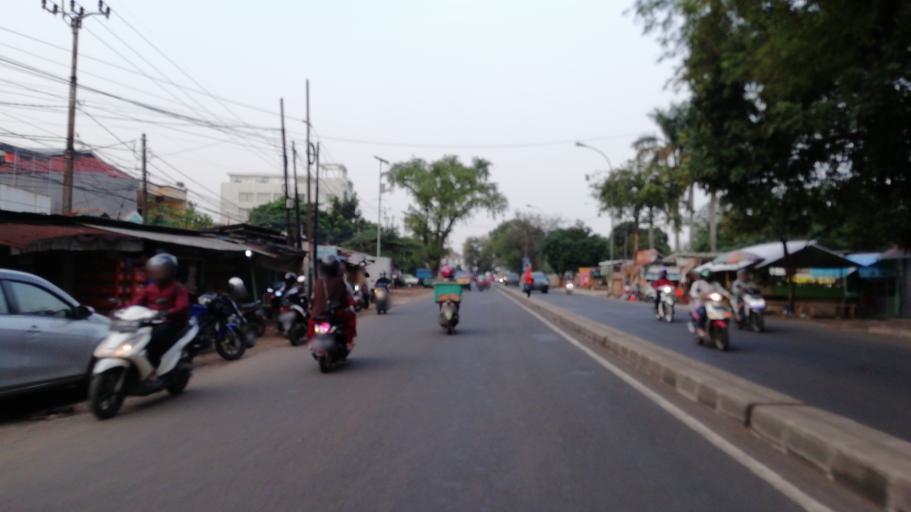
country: ID
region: West Java
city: Depok
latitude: -6.4143
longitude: 106.8597
